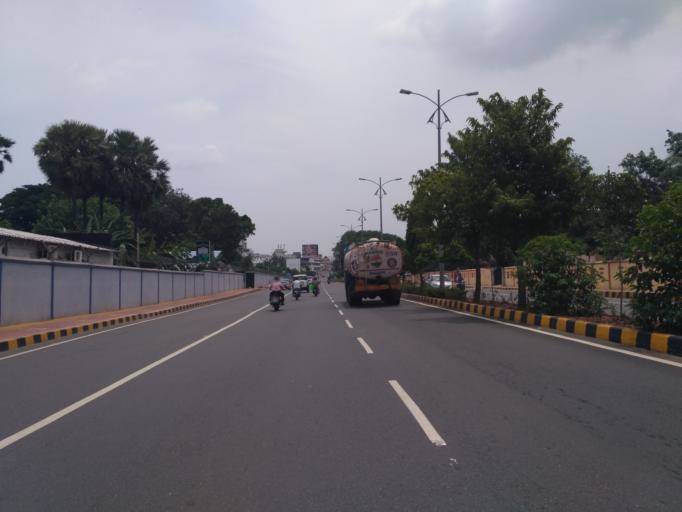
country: IN
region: Andhra Pradesh
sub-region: Vishakhapatnam
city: Yarada
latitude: 17.7240
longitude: 83.2944
